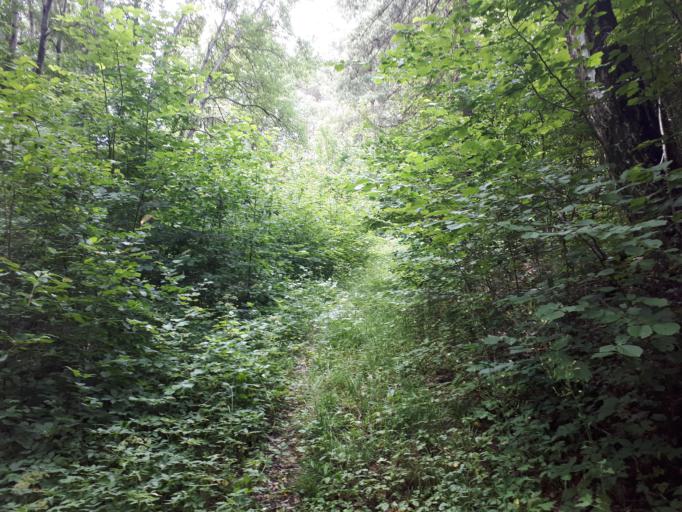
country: LT
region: Alytaus apskritis
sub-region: Alytus
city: Alytus
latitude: 54.3059
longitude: 23.9446
